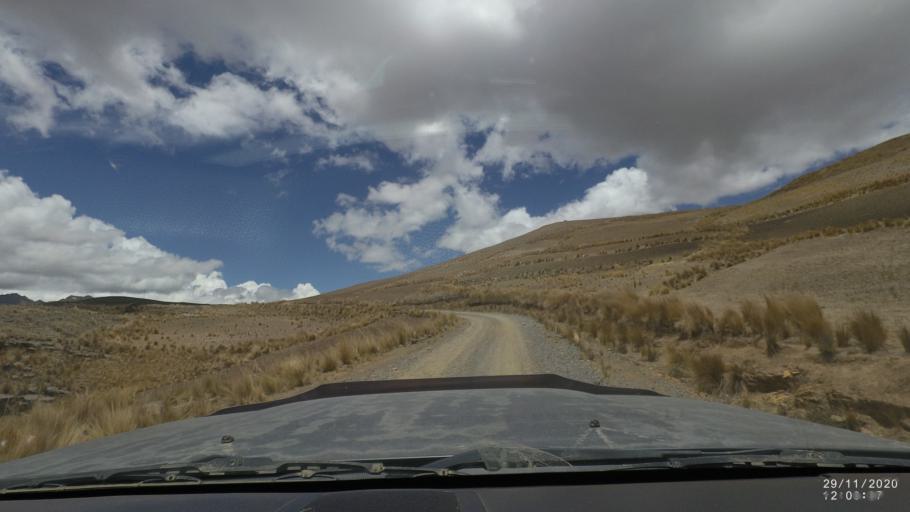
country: BO
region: Cochabamba
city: Cochabamba
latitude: -17.1501
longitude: -66.2863
